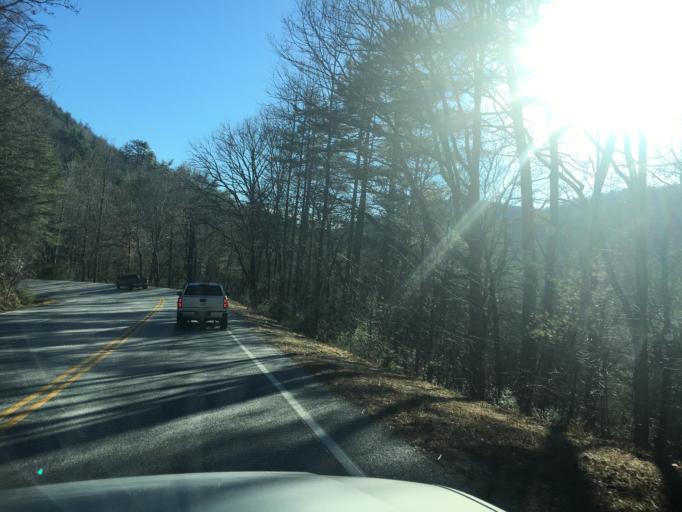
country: US
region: Georgia
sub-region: Union County
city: Blairsville
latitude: 34.7102
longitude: -83.9124
